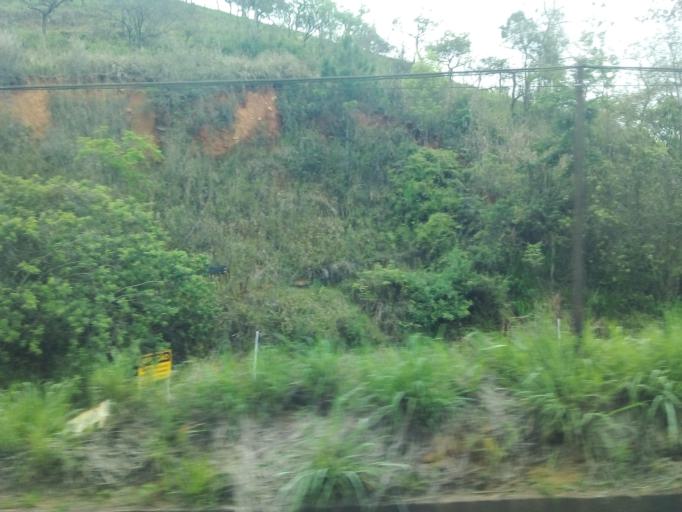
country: BR
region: Minas Gerais
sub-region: Nova Era
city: Nova Era
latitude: -19.7306
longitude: -42.9976
